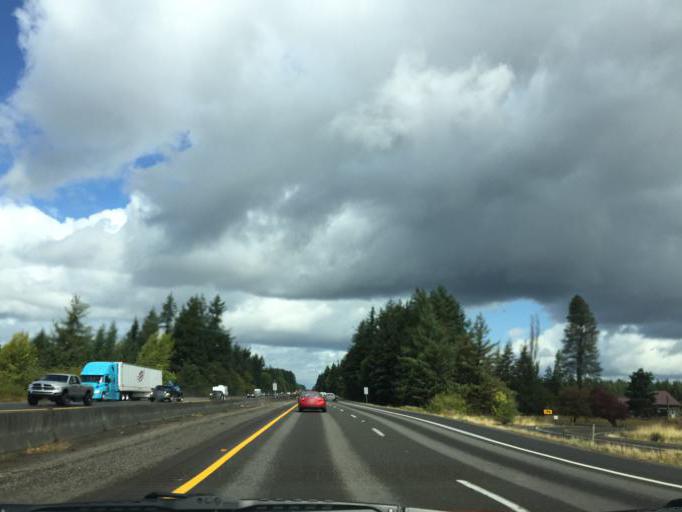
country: US
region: Washington
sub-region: Lewis County
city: Winlock
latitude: 46.5023
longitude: -122.8766
